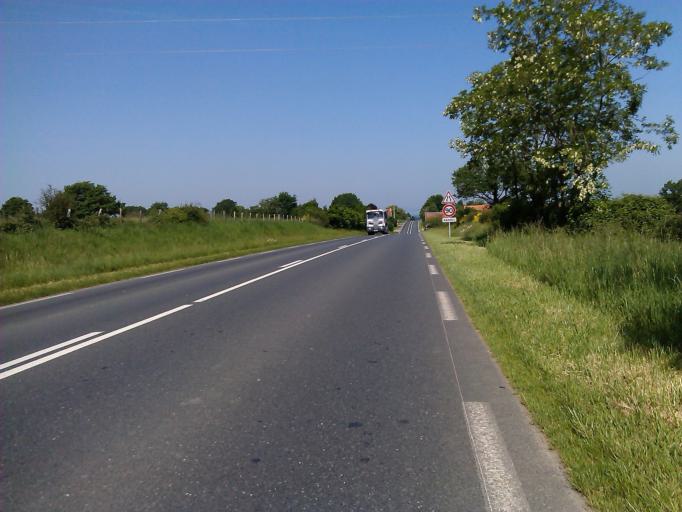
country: FR
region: Centre
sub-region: Departement de l'Indre
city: Cluis
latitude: 46.6049
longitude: 1.7145
